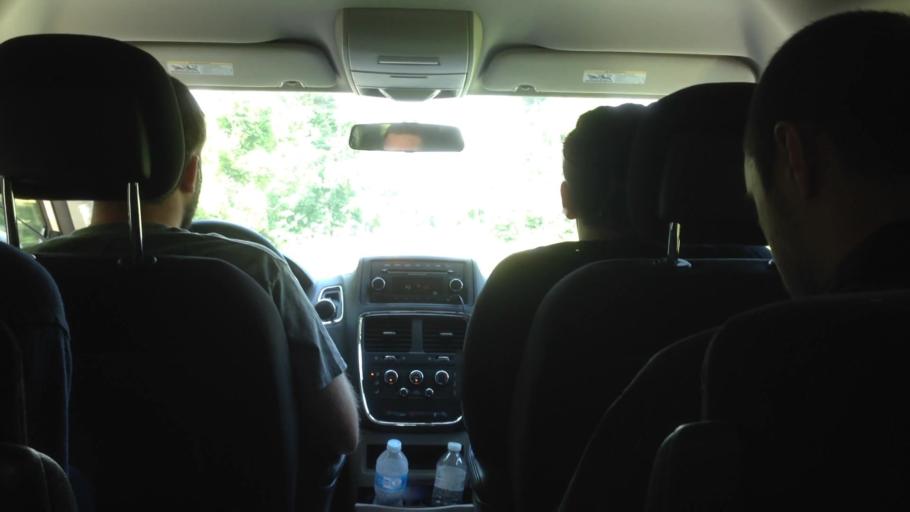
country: US
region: New York
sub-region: Dutchess County
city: Tivoli
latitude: 42.0941
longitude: -73.8959
